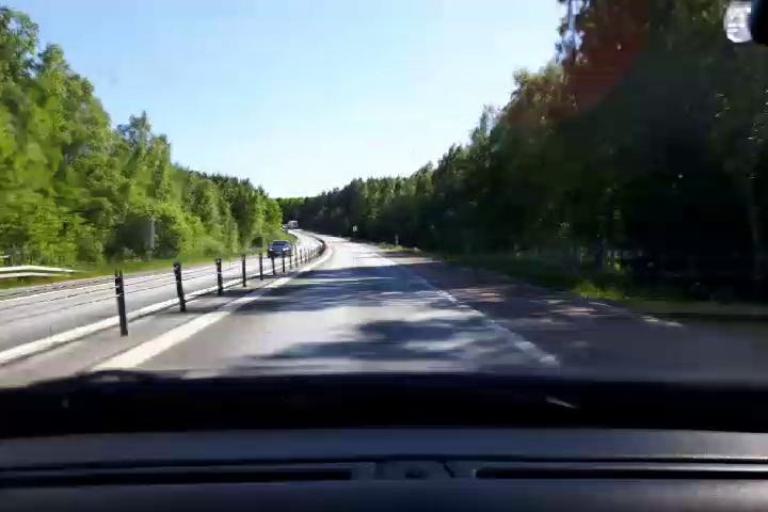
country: SE
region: Gaevleborg
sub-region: Soderhamns Kommun
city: Soderhamn
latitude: 61.2746
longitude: 17.0265
